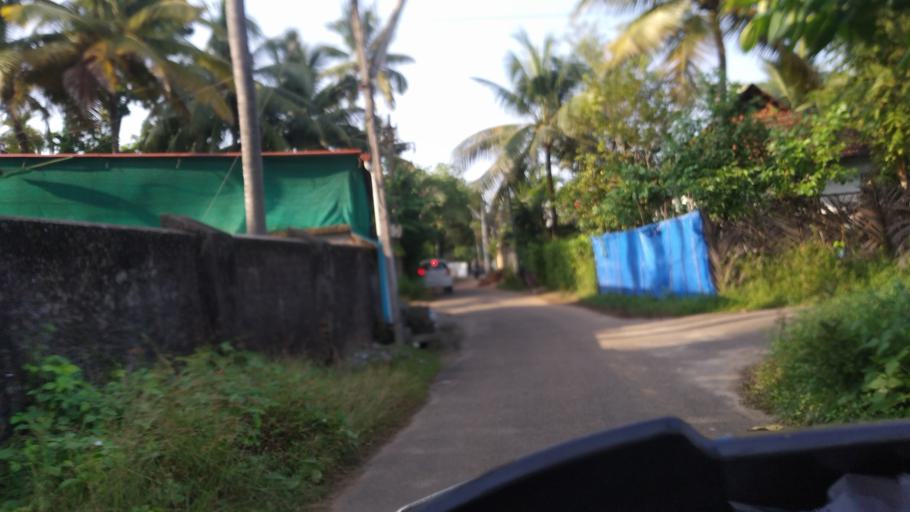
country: IN
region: Kerala
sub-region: Ernakulam
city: Elur
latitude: 10.0448
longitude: 76.2267
